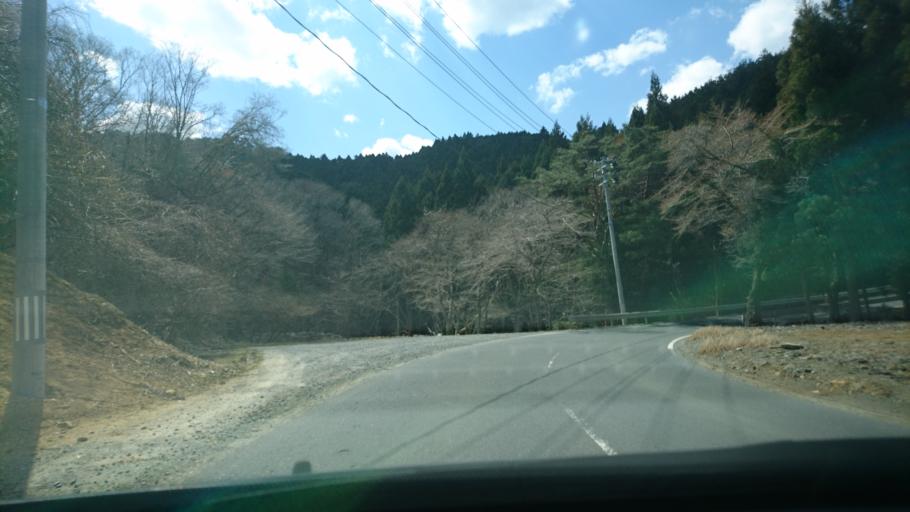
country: JP
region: Miyagi
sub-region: Oshika Gun
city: Onagawa Cho
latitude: 38.4606
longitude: 141.4840
